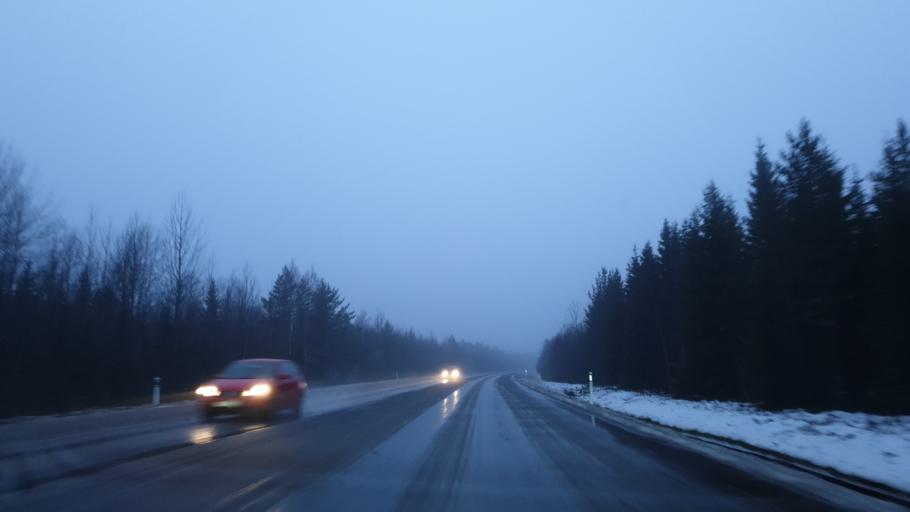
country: SE
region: Vaesterbotten
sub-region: Umea Kommun
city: Holmsund
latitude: 63.7568
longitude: 20.3524
